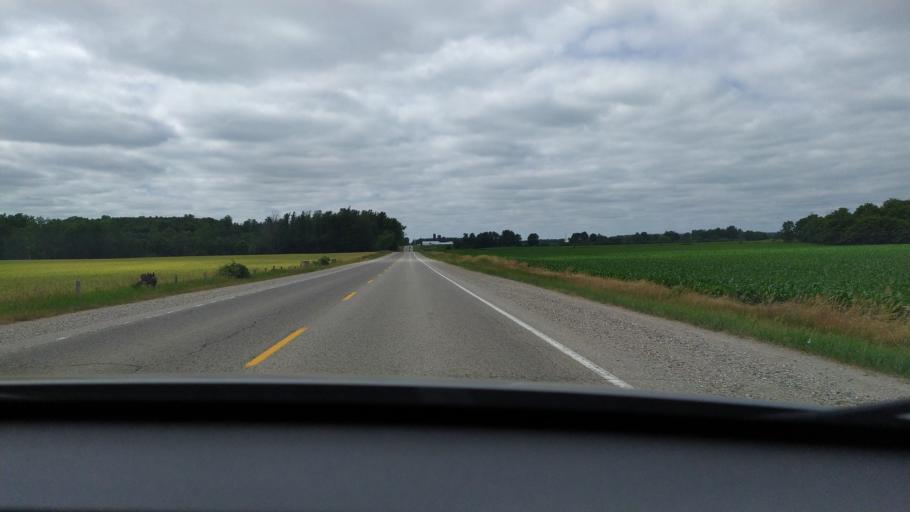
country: CA
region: Ontario
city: Stratford
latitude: 43.3206
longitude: -80.9541
